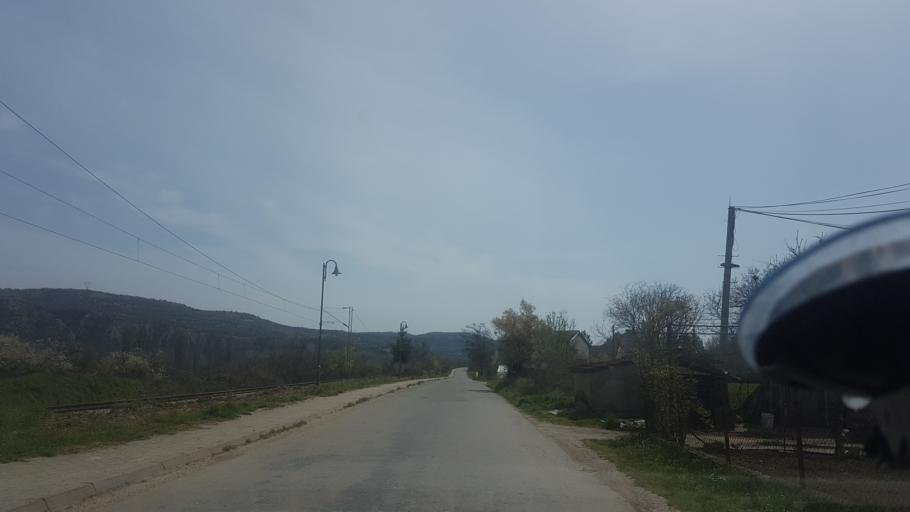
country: MK
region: Zelenikovo
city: Zelenikovo
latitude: 41.8835
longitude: 21.5908
